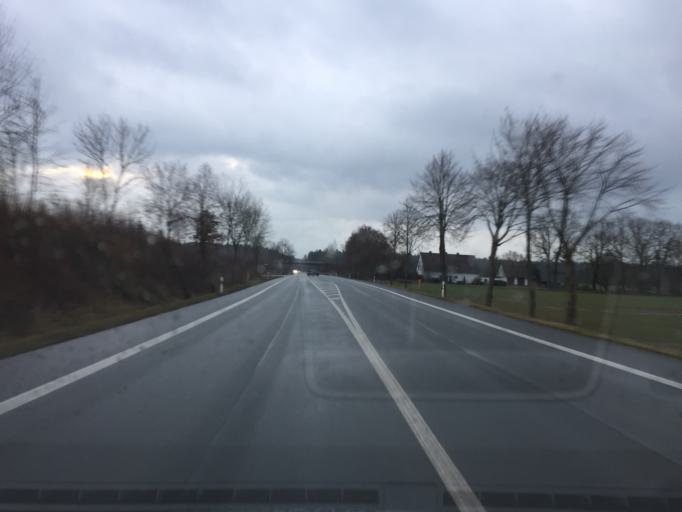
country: DE
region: North Rhine-Westphalia
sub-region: Regierungsbezirk Detmold
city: Petershagen
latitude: 52.3725
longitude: 8.9548
